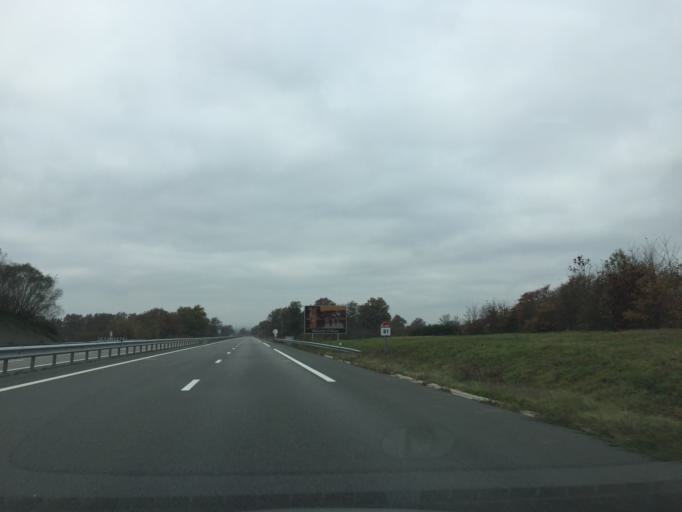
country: FR
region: Limousin
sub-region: Departement de la Creuse
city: Gouzon
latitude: 46.2314
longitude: 2.3120
